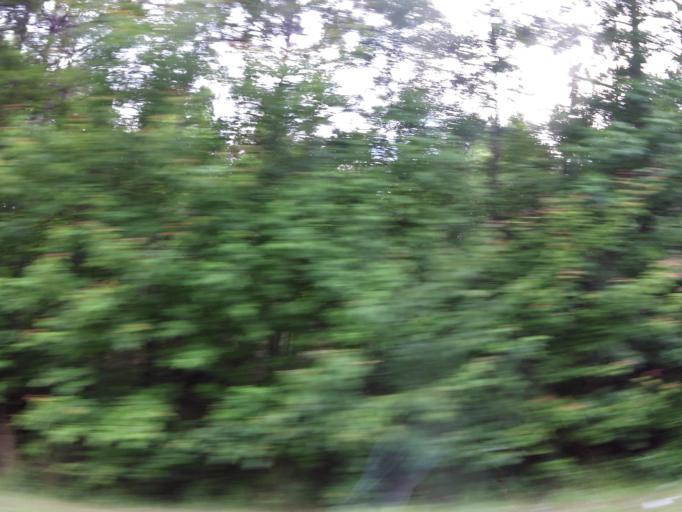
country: US
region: South Carolina
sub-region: Jasper County
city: Ridgeland
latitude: 32.4849
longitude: -81.1191
